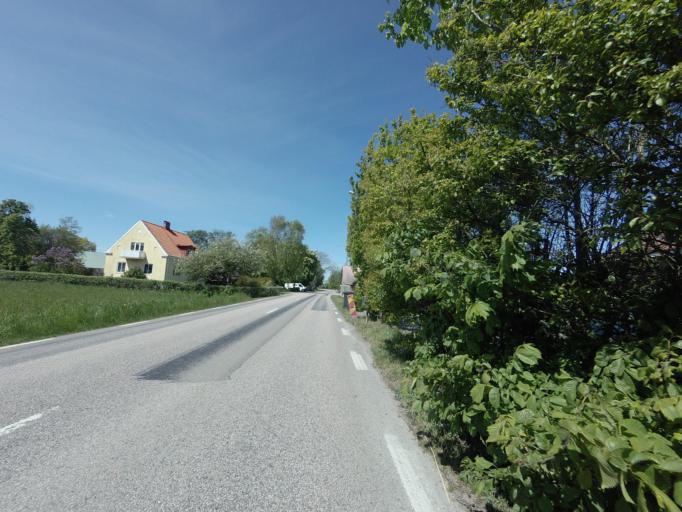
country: SE
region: Skane
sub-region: Helsingborg
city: Odakra
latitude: 56.1372
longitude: 12.6894
